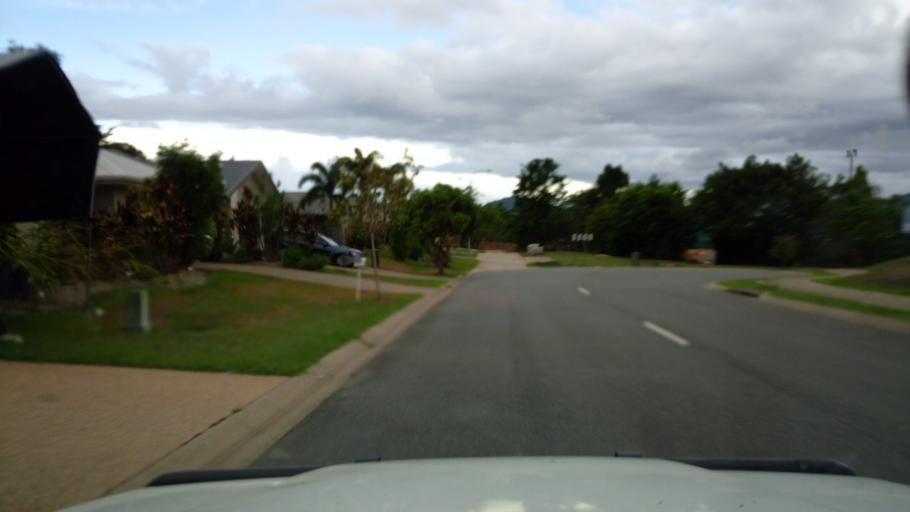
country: AU
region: Queensland
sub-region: Cairns
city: Redlynch
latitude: -16.8432
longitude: 145.6934
